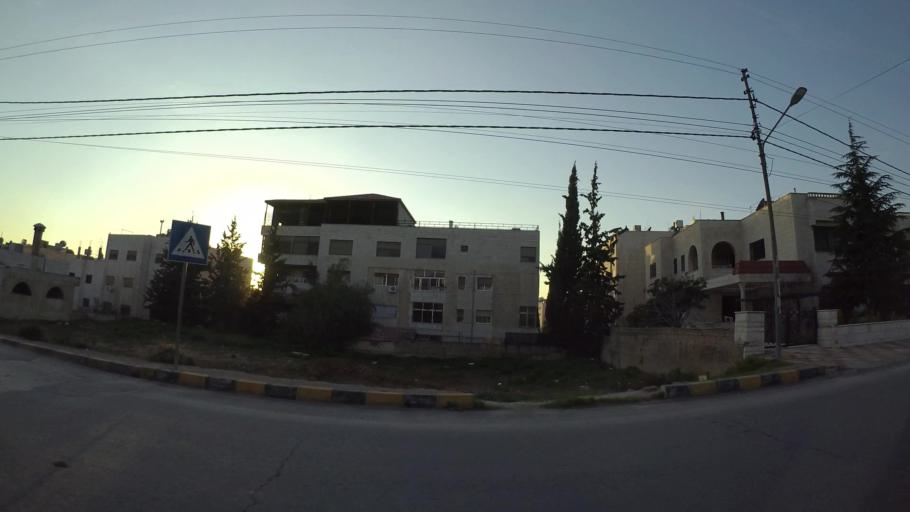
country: JO
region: Amman
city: Al Jubayhah
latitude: 31.9948
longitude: 35.8747
